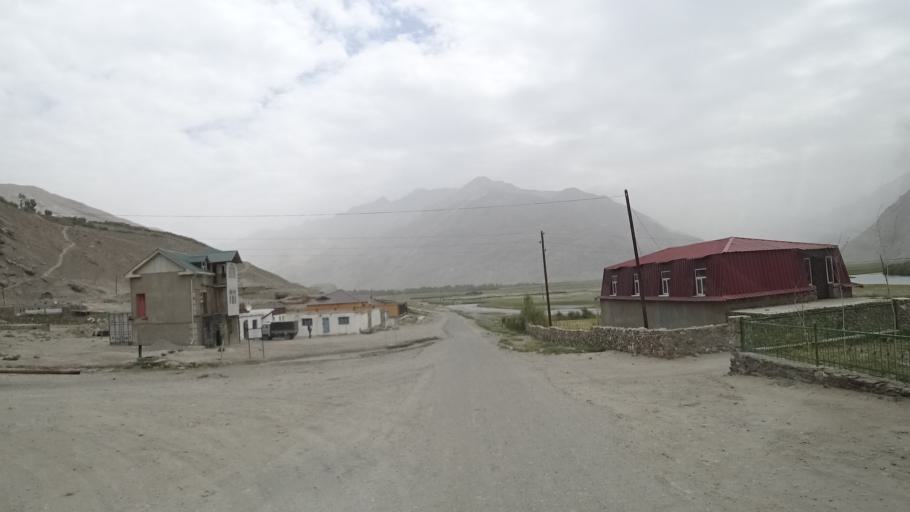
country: AF
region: Badakhshan
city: Khandud
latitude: 37.0320
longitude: 72.6311
